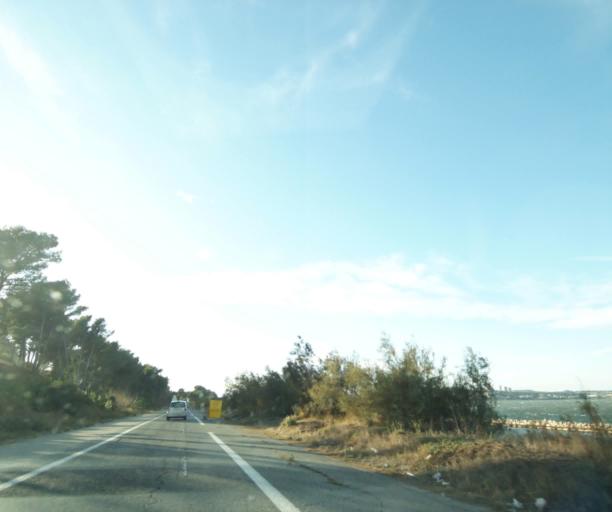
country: FR
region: Provence-Alpes-Cote d'Azur
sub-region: Departement des Bouches-du-Rhone
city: Martigues
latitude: 43.3987
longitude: 5.0808
